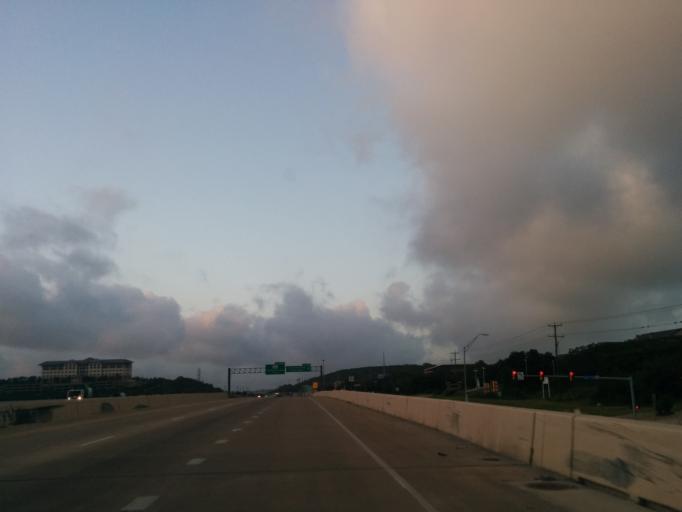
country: US
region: Texas
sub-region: Bexar County
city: Cross Mountain
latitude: 29.6253
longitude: -98.6102
